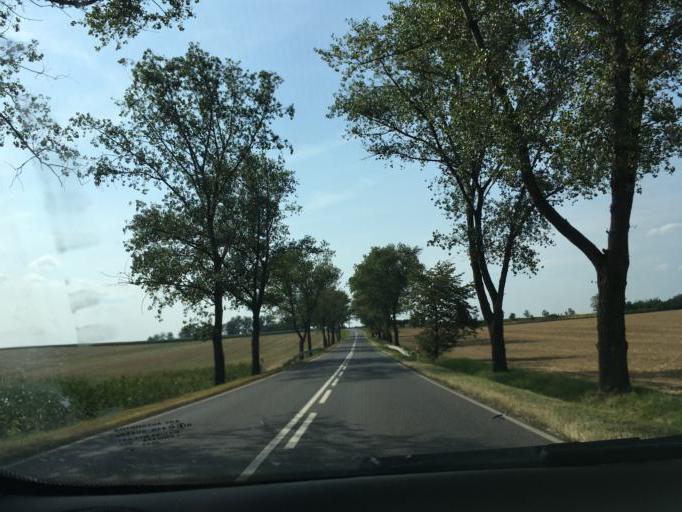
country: PL
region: Opole Voivodeship
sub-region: Powiat prudnicki
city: Moszczanka
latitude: 50.4213
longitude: 17.4631
